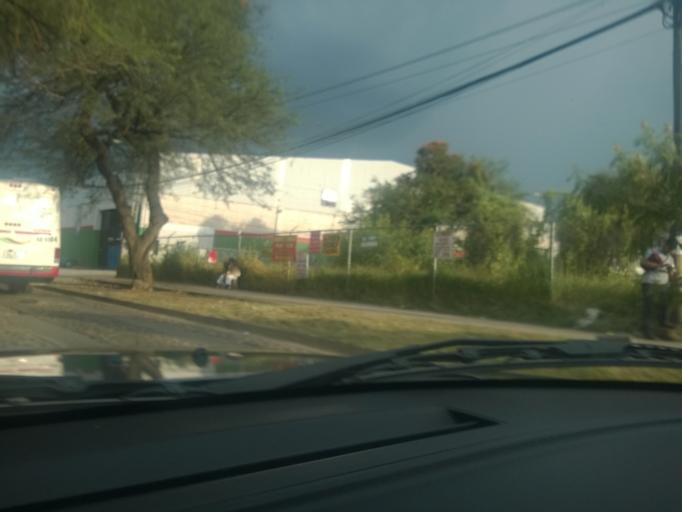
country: MX
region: Guanajuato
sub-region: Leon
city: Medina
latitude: 21.1135
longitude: -101.6193
